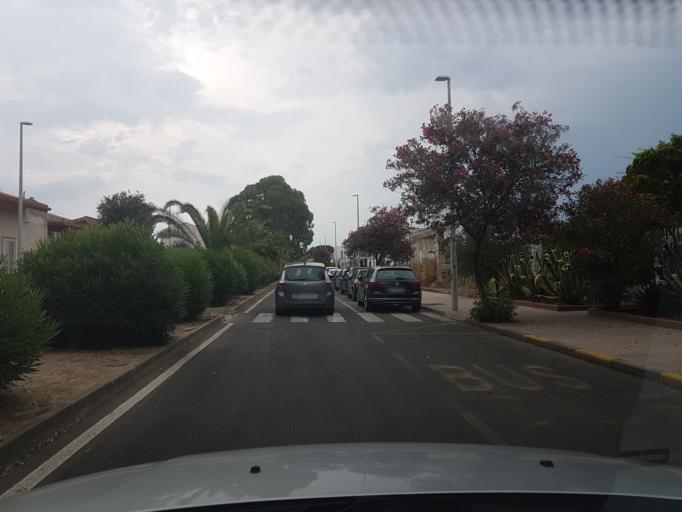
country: IT
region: Sardinia
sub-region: Provincia di Oristano
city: Cabras
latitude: 39.9072
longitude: 8.5153
